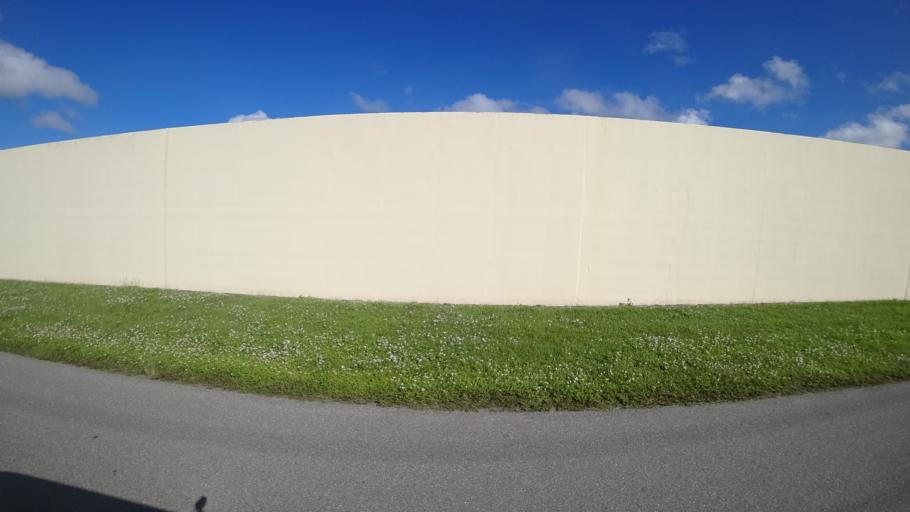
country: US
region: Florida
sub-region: Manatee County
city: Ellenton
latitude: 27.5841
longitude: -82.4760
